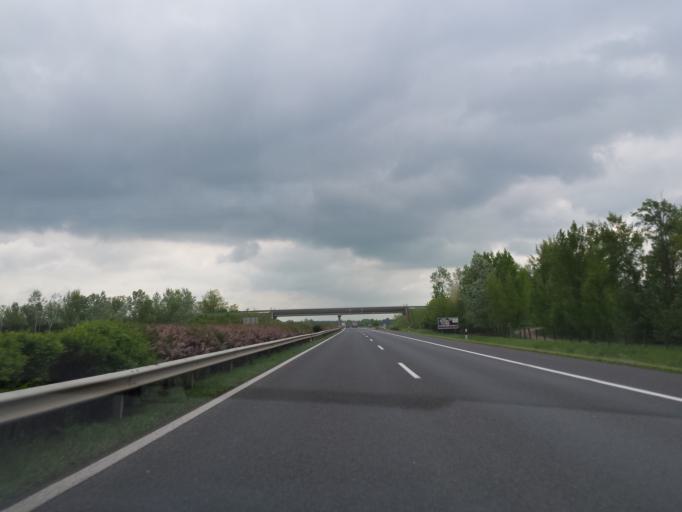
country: HU
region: Gyor-Moson-Sopron
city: Otteveny
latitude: 47.7011
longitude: 17.4989
